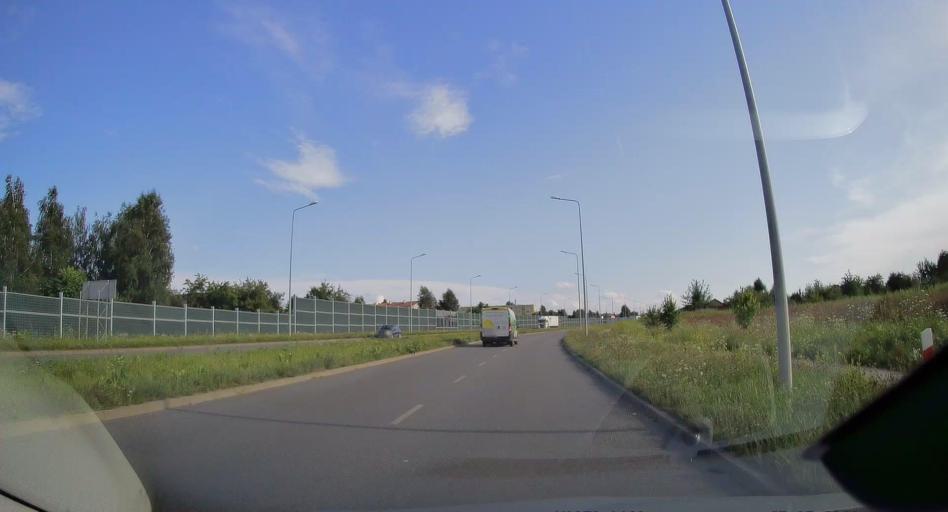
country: PL
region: Swietokrzyskie
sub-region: Powiat konecki
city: Konskie
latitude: 51.1985
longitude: 20.4000
